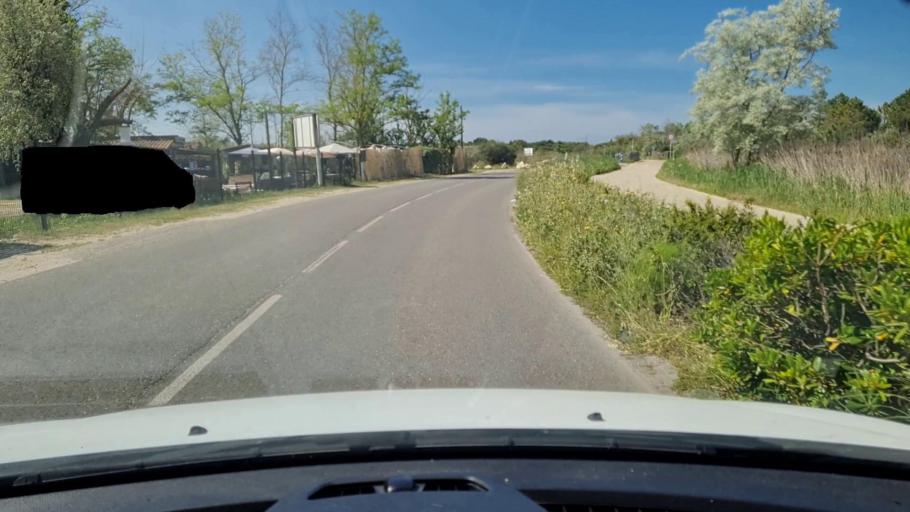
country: FR
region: Languedoc-Roussillon
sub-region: Departement du Gard
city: Le Grau-du-Roi
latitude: 43.5024
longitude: 4.1418
